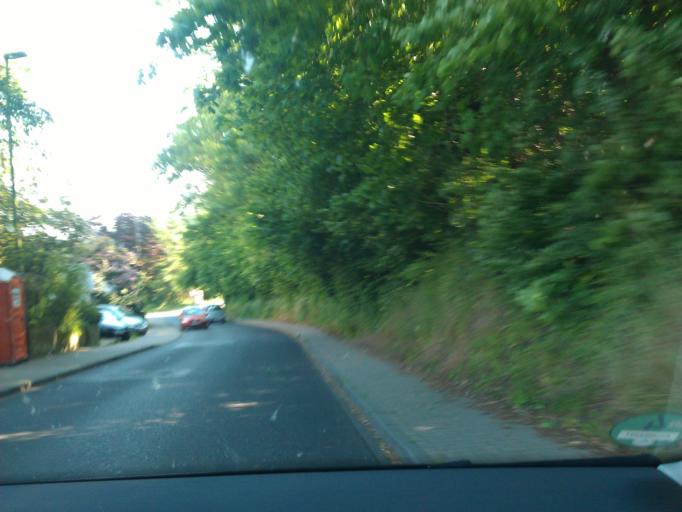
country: DE
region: North Rhine-Westphalia
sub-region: Regierungsbezirk Koln
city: Aachen
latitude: 50.7972
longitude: 6.0539
